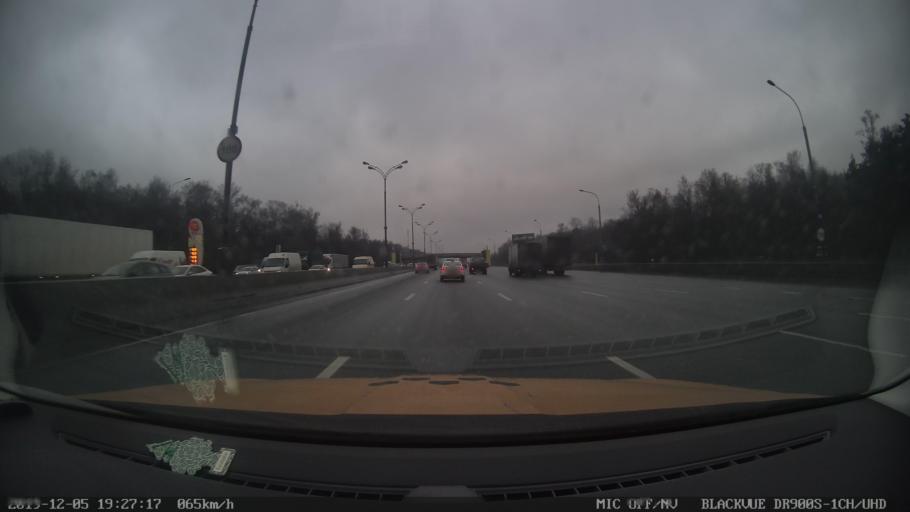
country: RU
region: Moscow
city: Vatutino
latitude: 55.8954
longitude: 37.6614
